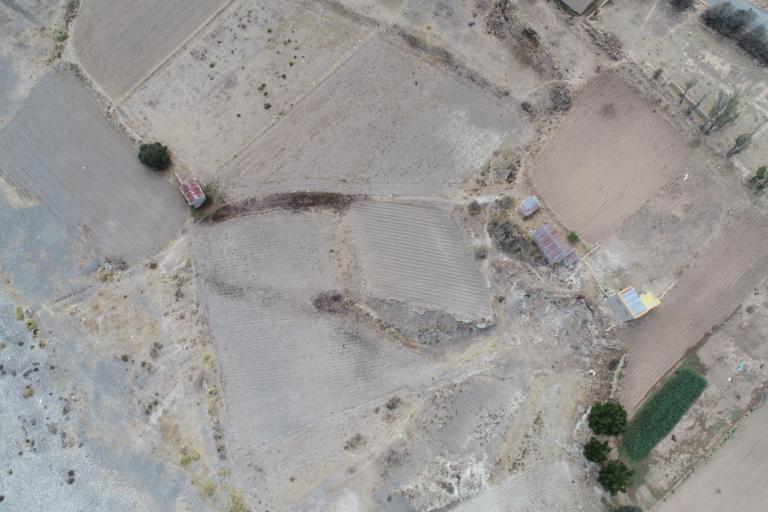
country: BO
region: La Paz
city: Achacachi
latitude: -16.0405
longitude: -68.6812
